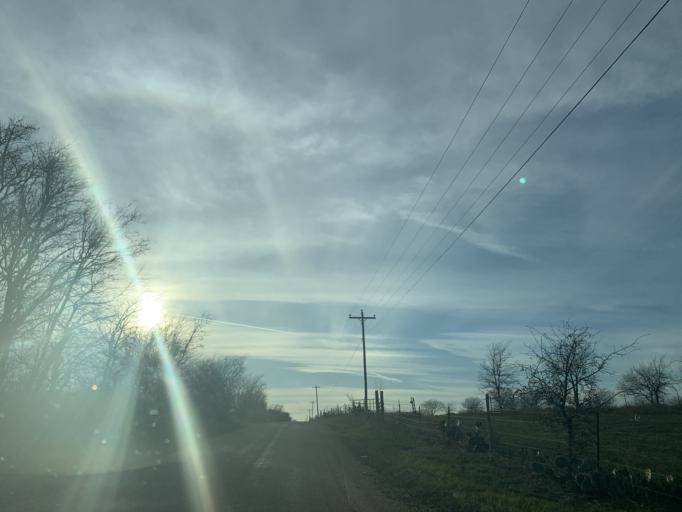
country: US
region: Texas
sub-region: Bell County
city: Salado
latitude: 30.8757
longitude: -97.5840
